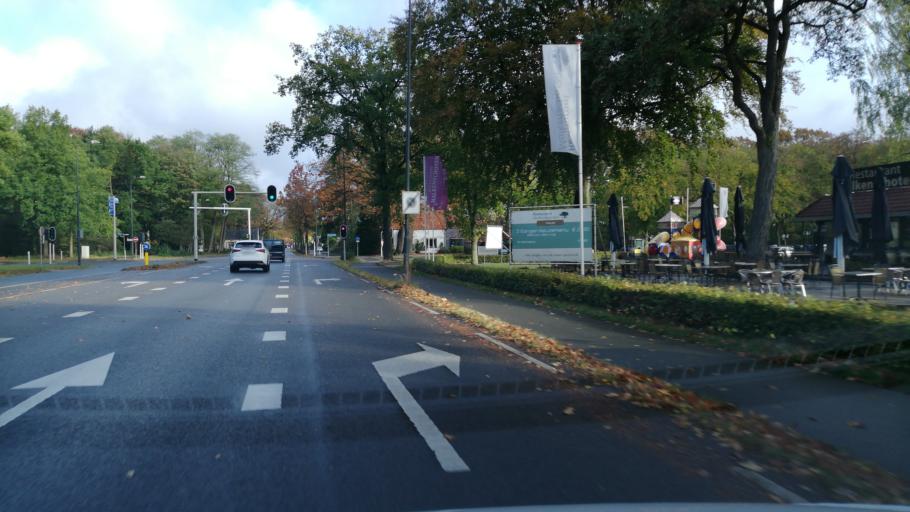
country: NL
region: Gelderland
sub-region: Gemeente Apeldoorn
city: Beekbergen
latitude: 52.1839
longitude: 5.9622
